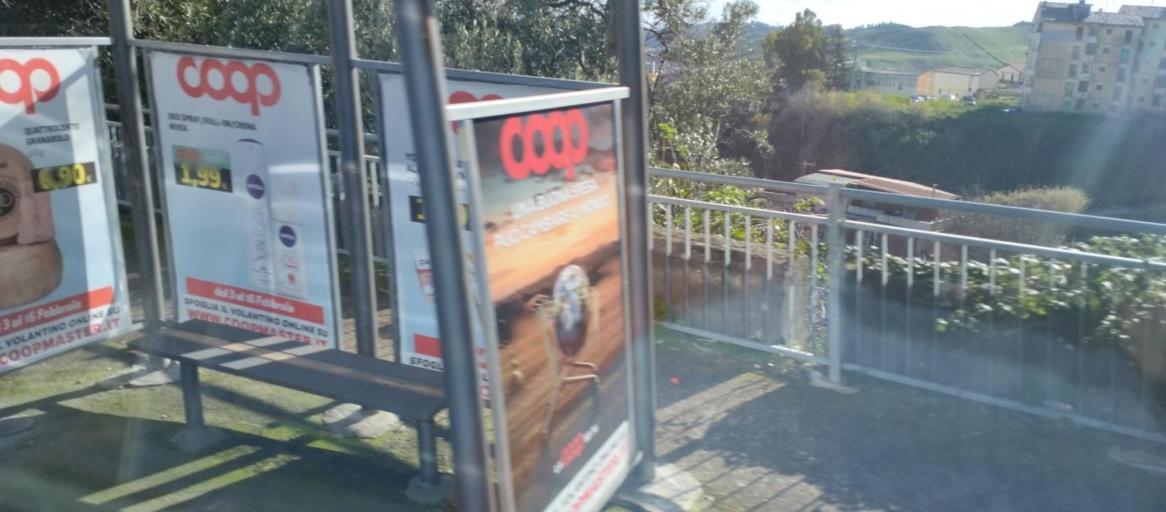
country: IT
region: Calabria
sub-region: Provincia di Catanzaro
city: Catanzaro
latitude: 38.8991
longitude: 16.5978
